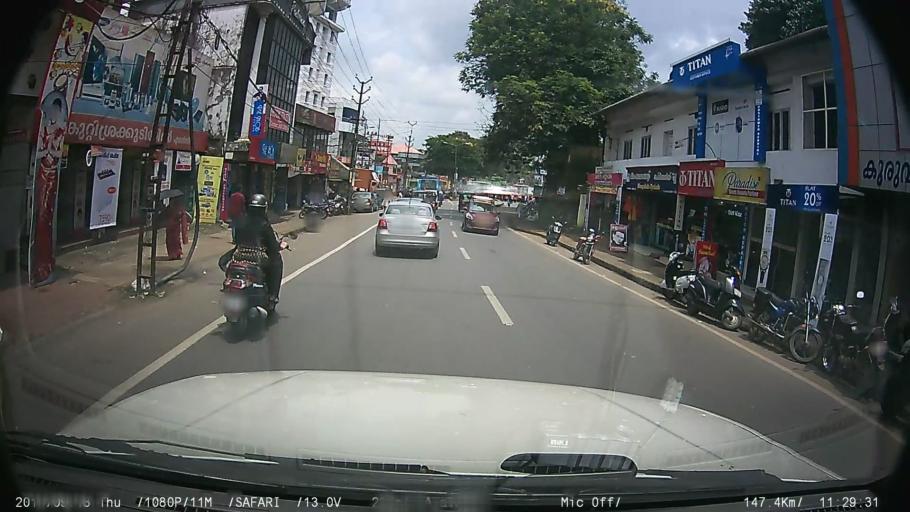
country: IN
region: Kerala
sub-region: Ernakulam
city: Muvattupula
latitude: 9.9855
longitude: 76.5784
